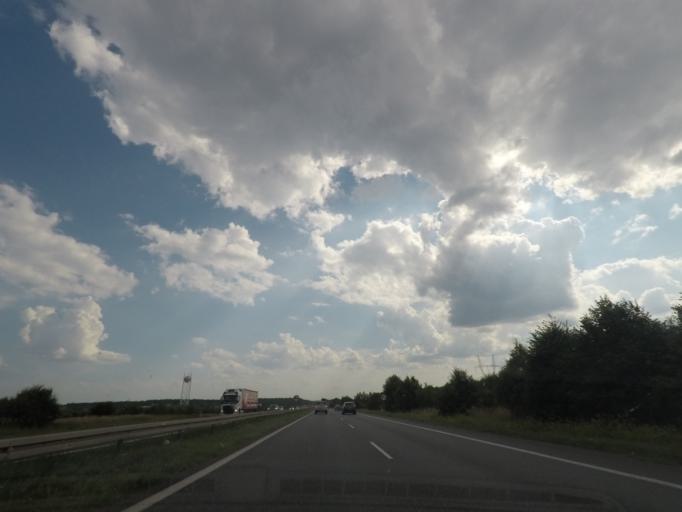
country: PL
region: Lodz Voivodeship
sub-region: Powiat radomszczanski
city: Radomsko
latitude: 51.0875
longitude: 19.3750
